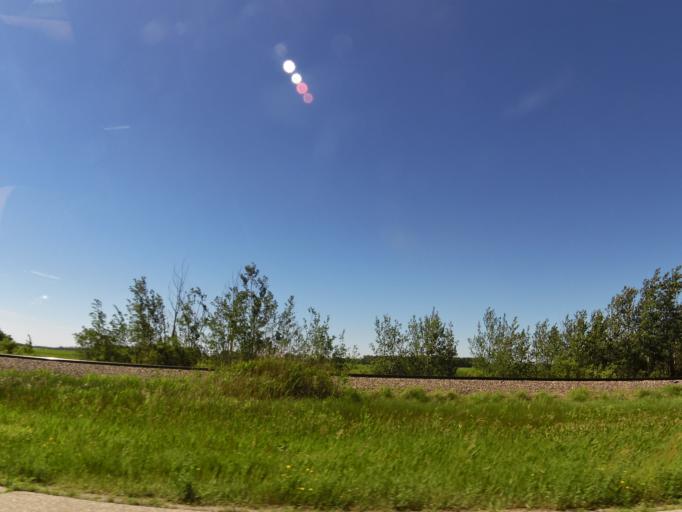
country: US
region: Minnesota
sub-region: Red Lake County
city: Red Lake Falls
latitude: 47.6898
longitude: -96.0787
